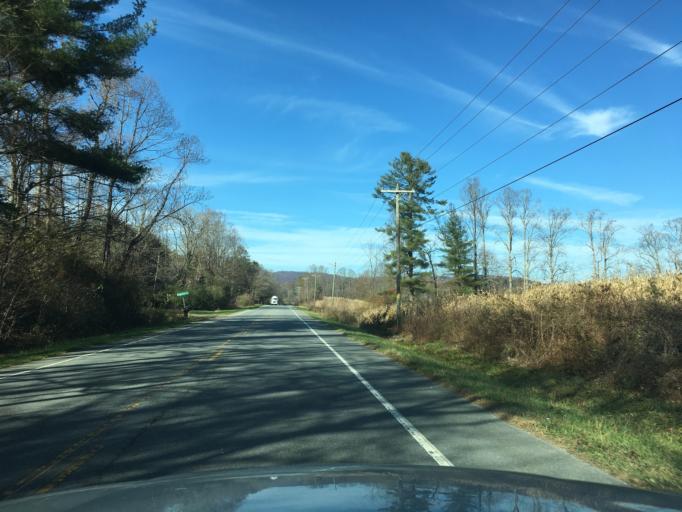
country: US
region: North Carolina
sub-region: Henderson County
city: Etowah
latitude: 35.2917
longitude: -82.6250
